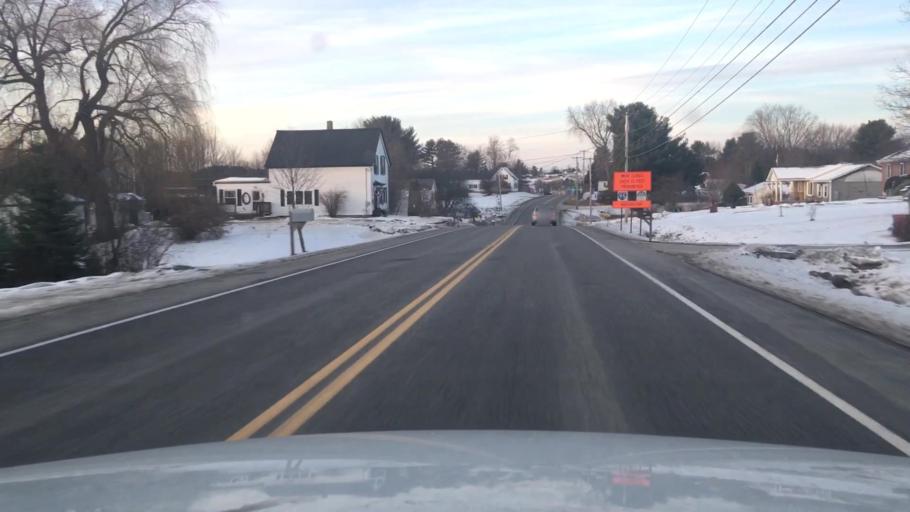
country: US
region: Maine
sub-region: Androscoggin County
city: Sabattus
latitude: 44.0974
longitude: -70.0845
